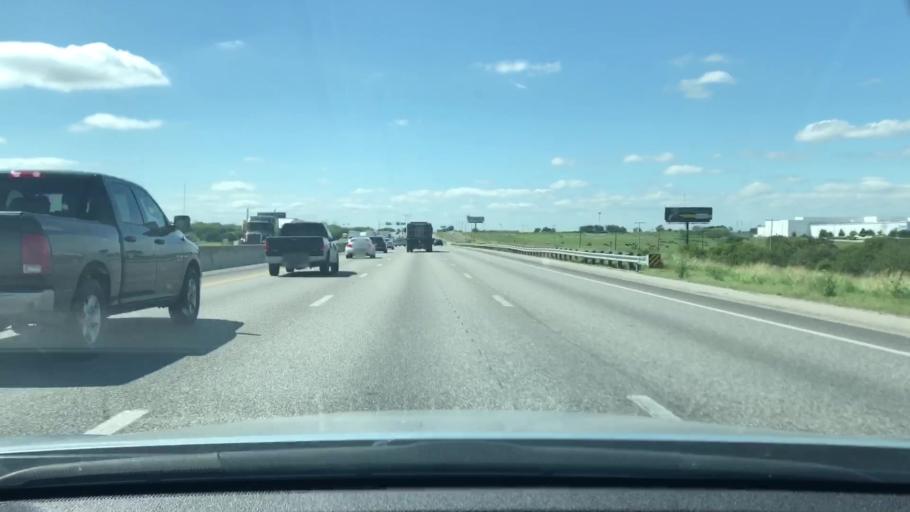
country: US
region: Texas
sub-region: Guadalupe County
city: Northcliff
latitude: 29.6412
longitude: -98.2095
